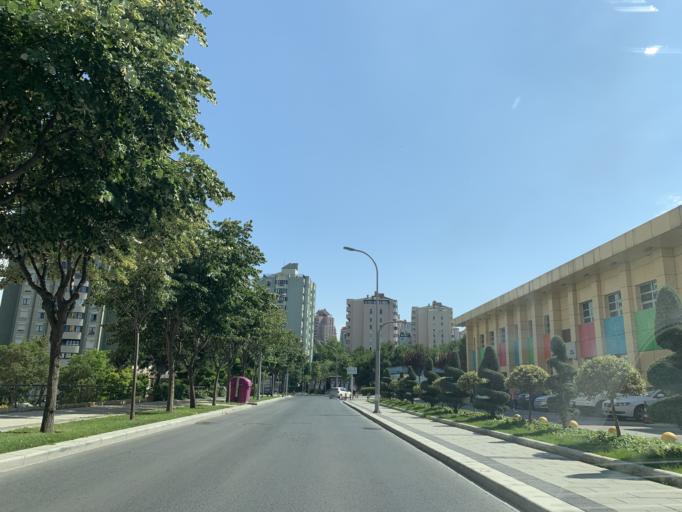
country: TR
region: Istanbul
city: Esenyurt
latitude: 41.0684
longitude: 28.6778
